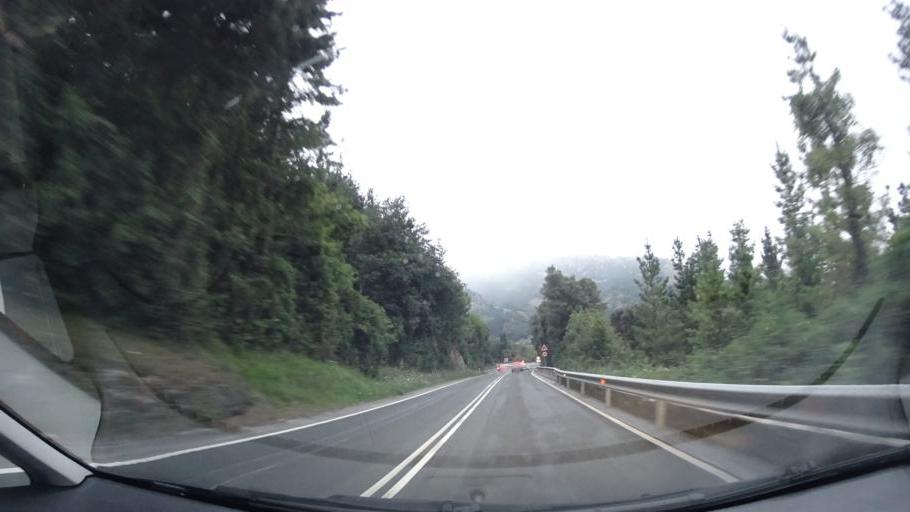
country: ES
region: Basque Country
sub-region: Bizkaia
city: Manaria
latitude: 43.1284
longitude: -2.6620
